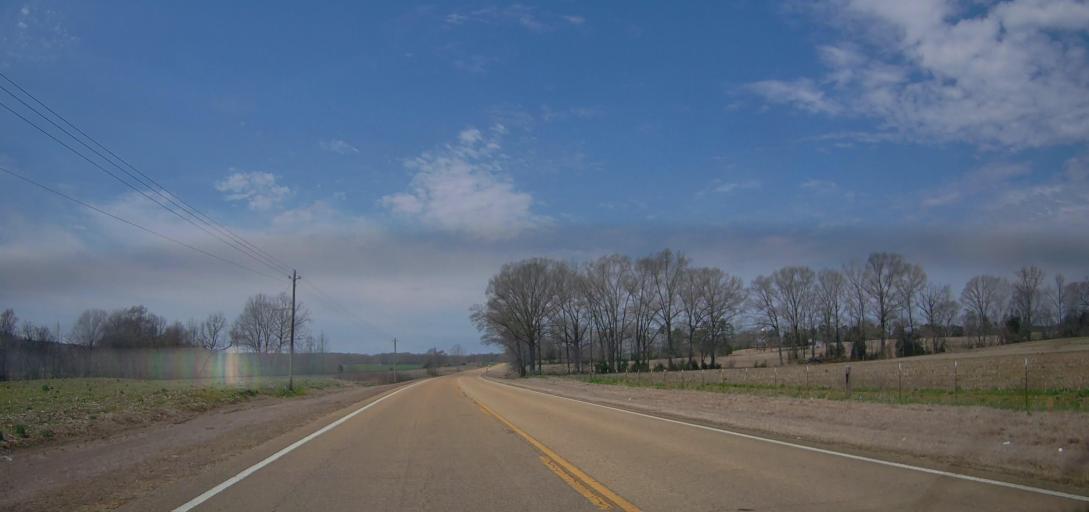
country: US
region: Mississippi
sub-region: Benton County
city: Ashland
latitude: 34.6191
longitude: -89.2223
